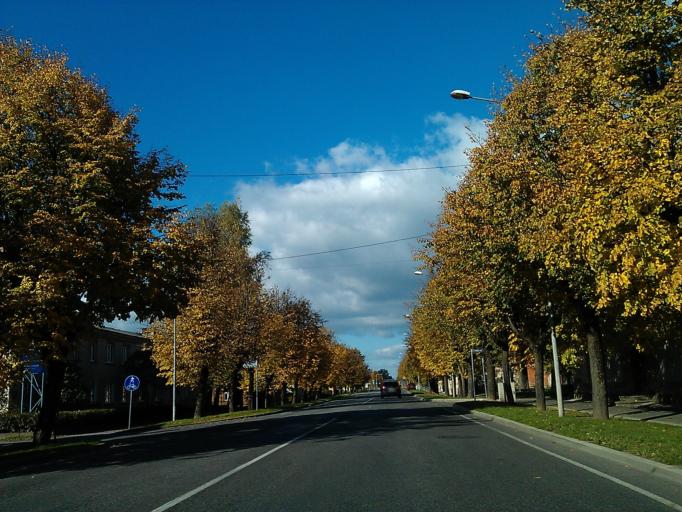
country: LV
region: Livani
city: Livani
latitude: 56.3642
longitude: 26.1704
